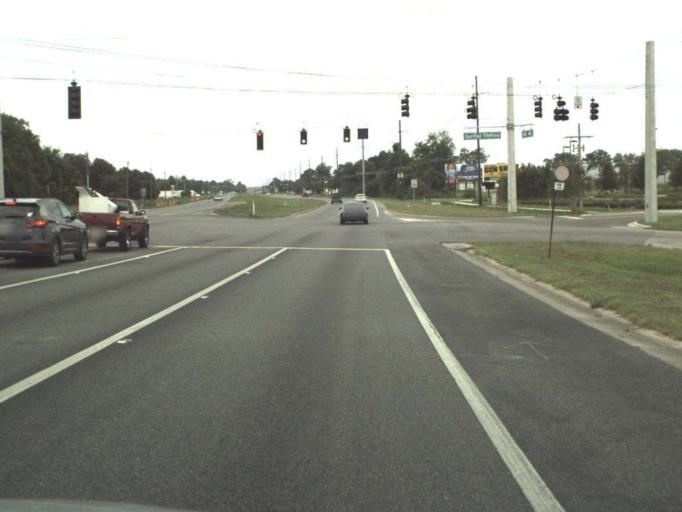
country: US
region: Florida
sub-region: Seminole County
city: Sanford
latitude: 28.8113
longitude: -81.2974
